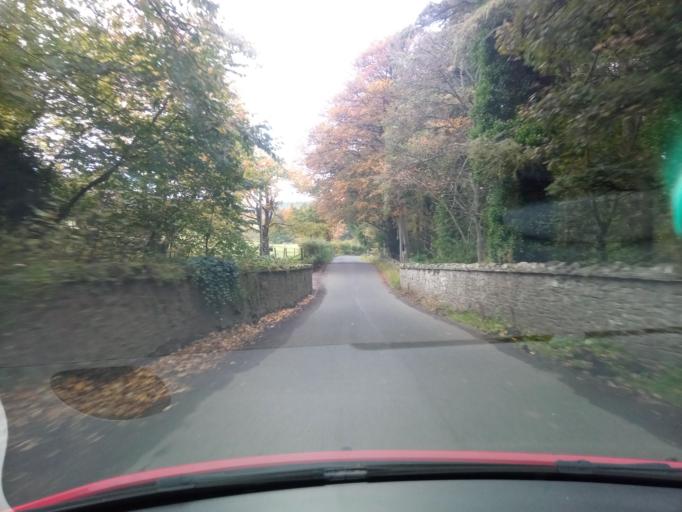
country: GB
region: Scotland
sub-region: The Scottish Borders
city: Peebles
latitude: 55.6333
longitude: -3.1429
